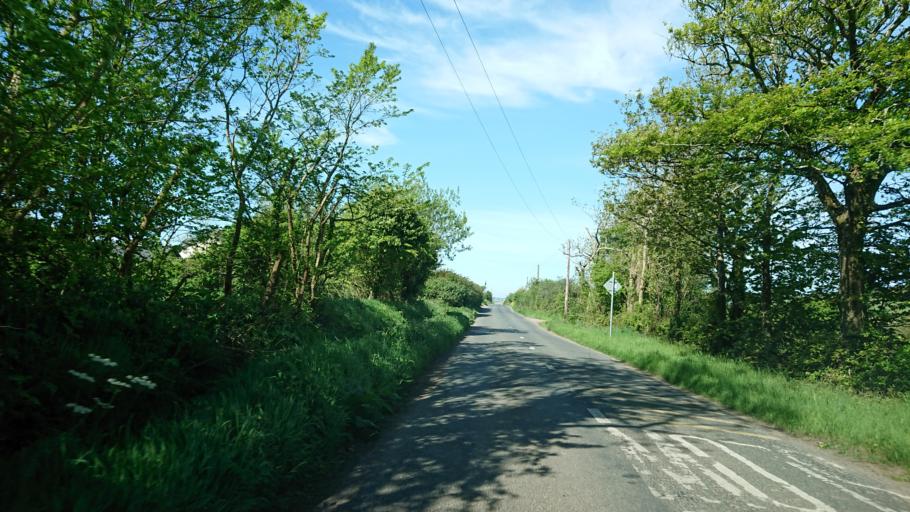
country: IE
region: Munster
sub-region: Waterford
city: Dunmore East
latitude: 52.1783
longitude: -7.0154
